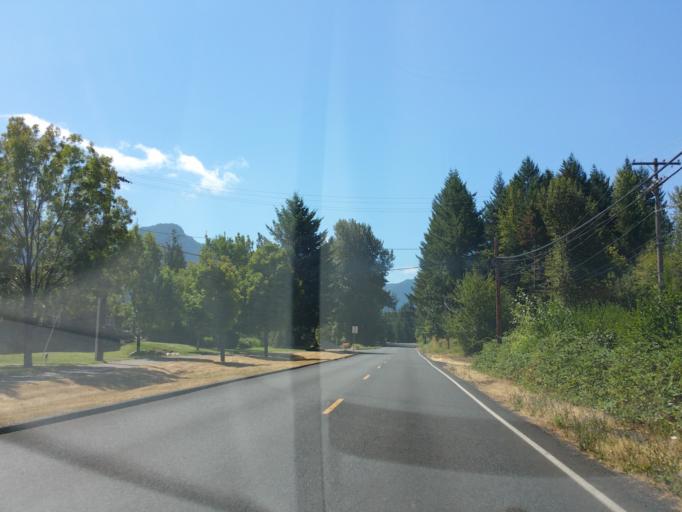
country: US
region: Washington
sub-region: Skamania County
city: Stevenson
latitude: 45.6884
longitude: -121.8995
